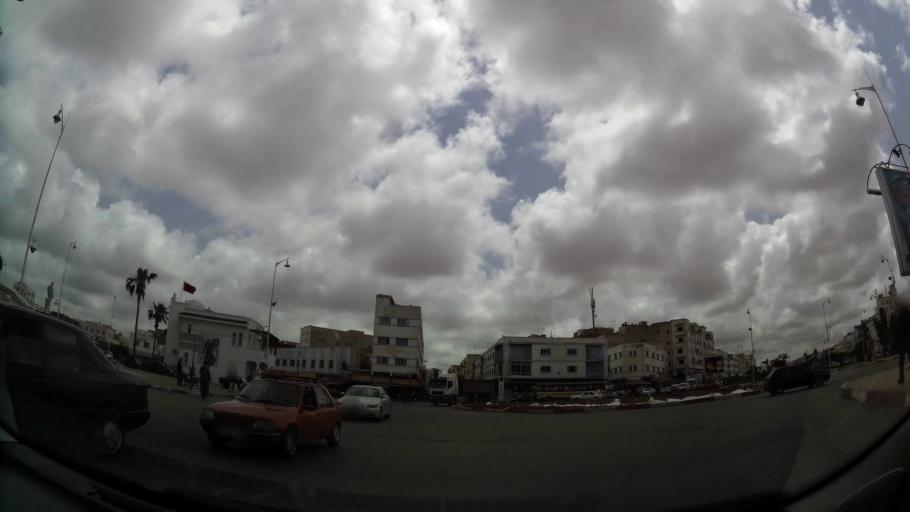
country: MA
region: Oriental
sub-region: Nador
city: Nador
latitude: 35.1796
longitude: -2.9279
